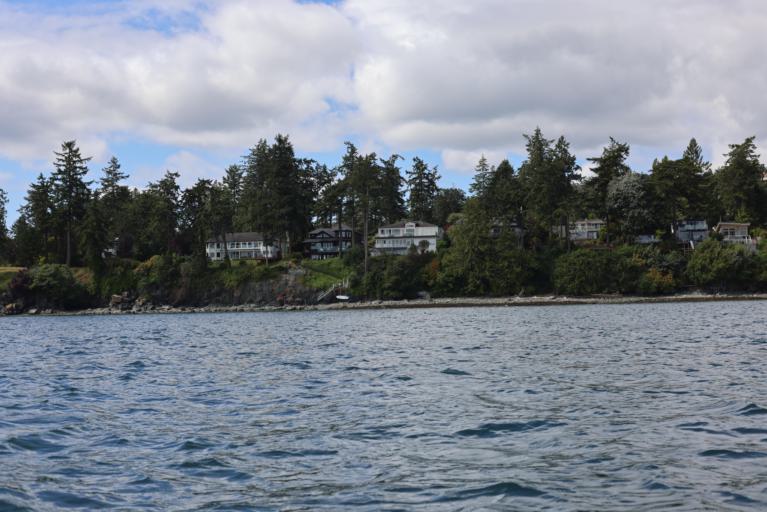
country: CA
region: British Columbia
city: Victoria
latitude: 48.5152
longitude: -123.3594
